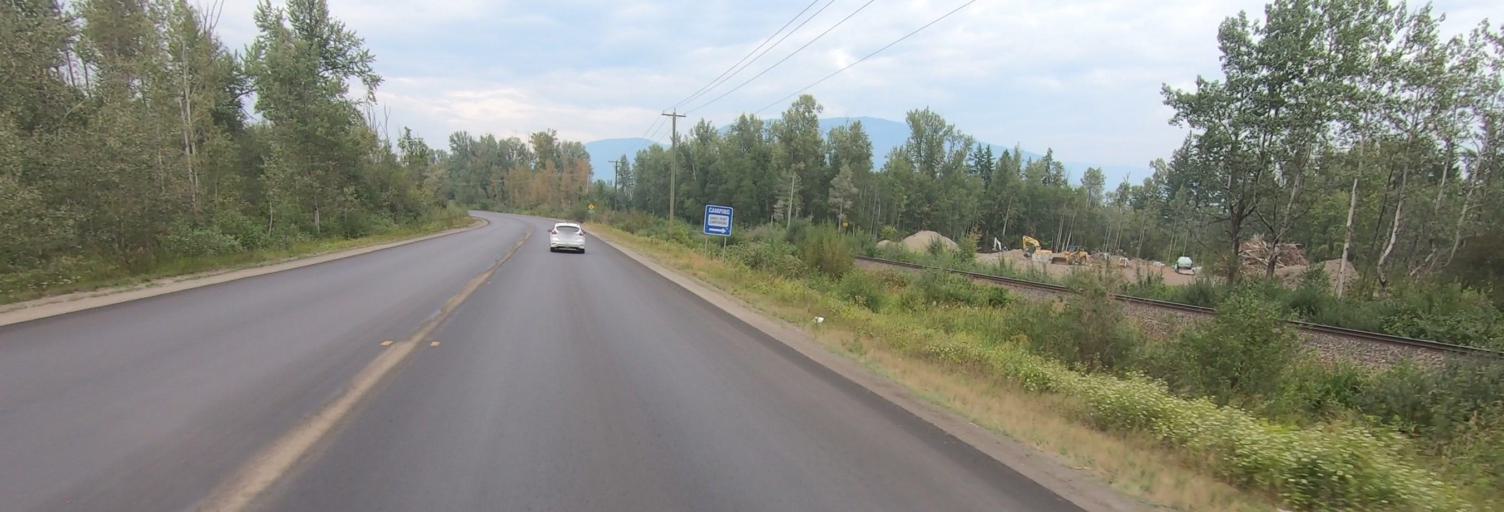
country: CA
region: British Columbia
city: Salmon Arm
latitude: 50.7285
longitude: -119.3159
